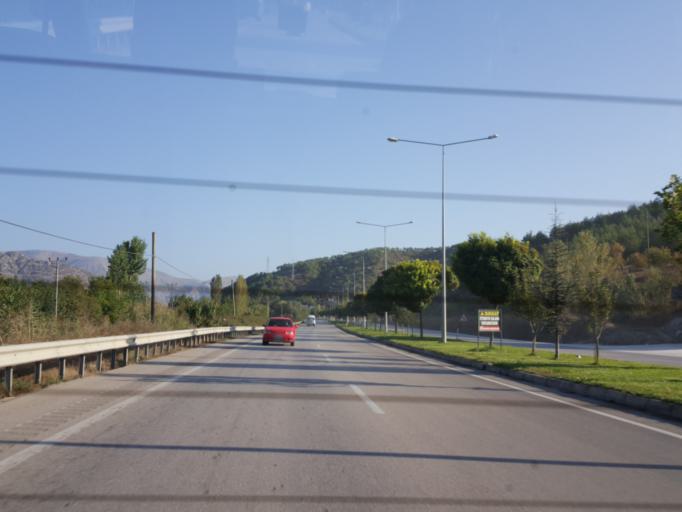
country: TR
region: Amasya
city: Amasya
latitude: 40.5749
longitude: 35.7880
